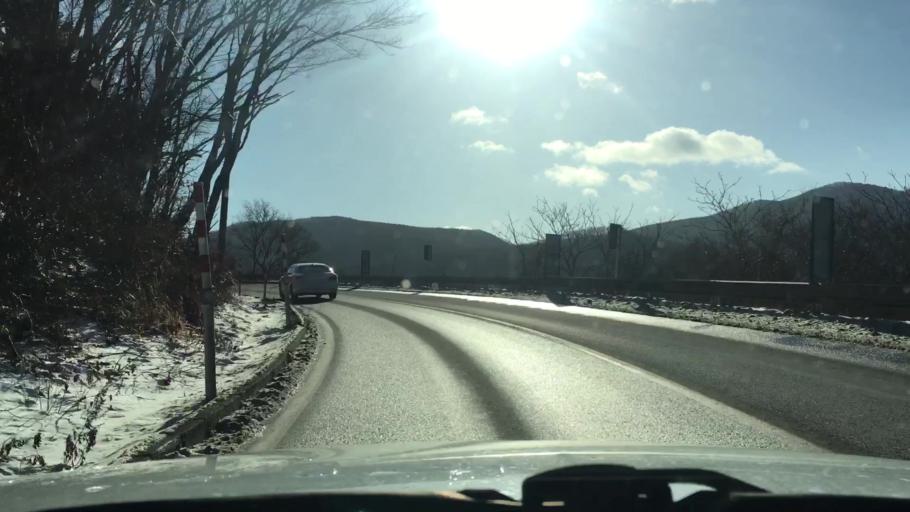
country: JP
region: Iwate
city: Morioka-shi
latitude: 39.6631
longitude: 141.3273
